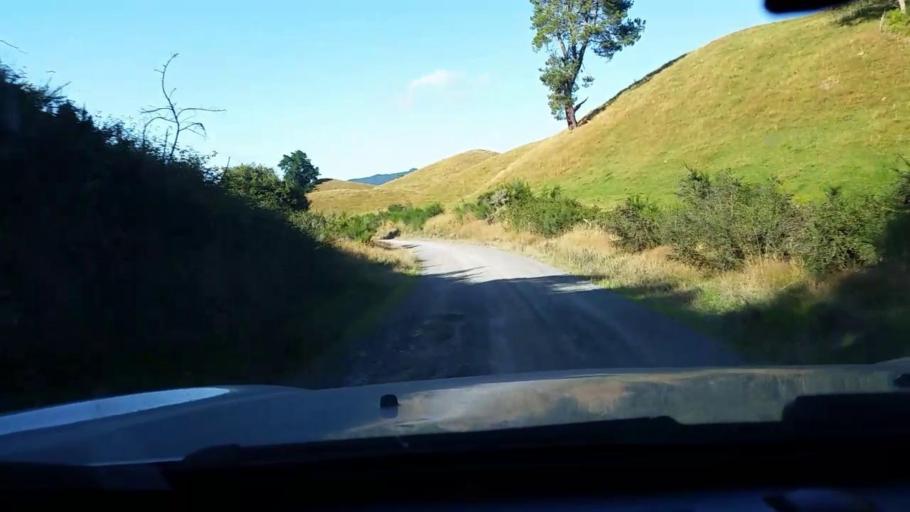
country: NZ
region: Waikato
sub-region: Taupo District
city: Taupo
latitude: -38.4905
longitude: 176.2081
